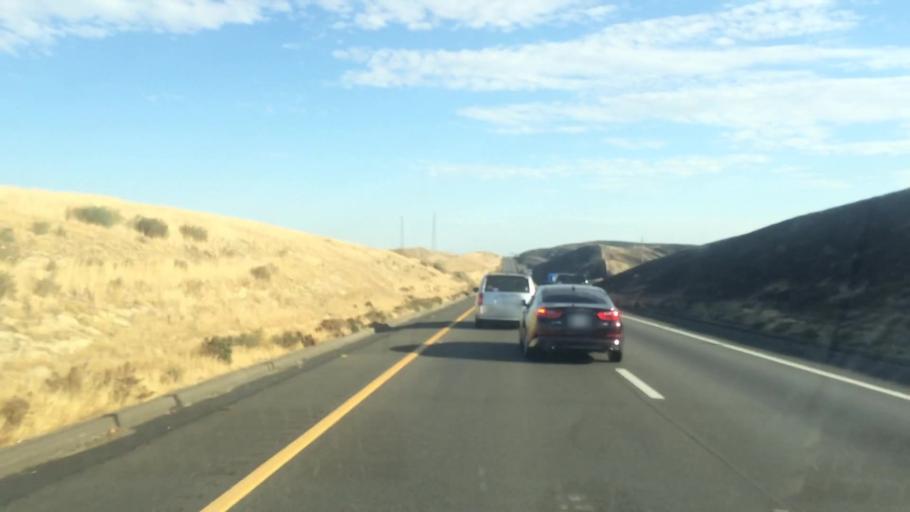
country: US
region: California
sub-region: Kings County
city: Kettleman City
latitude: 35.9946
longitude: -119.9738
